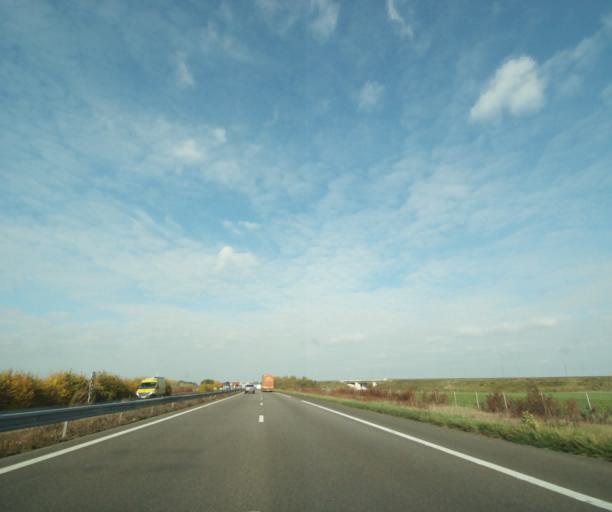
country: FR
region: Champagne-Ardenne
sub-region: Departement de la Marne
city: Verzy
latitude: 49.1077
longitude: 4.2540
